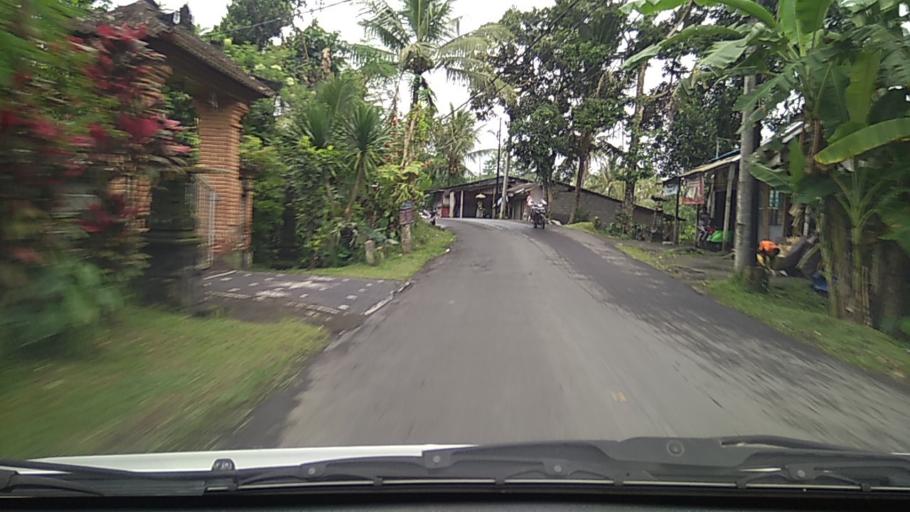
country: ID
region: Bali
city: Banjar Dujung Kaja
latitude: -8.4094
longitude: 115.2914
